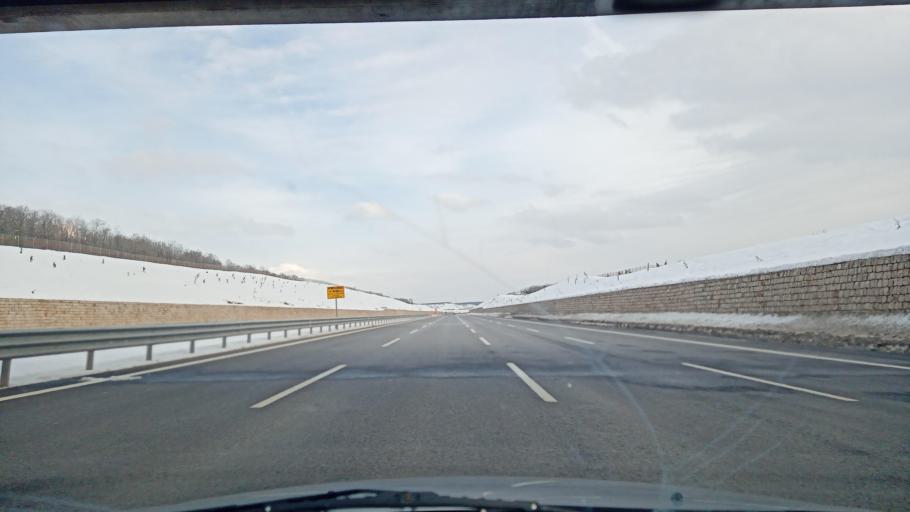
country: TR
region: Kocaeli
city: Mollafeneri
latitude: 40.8905
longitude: 29.5951
